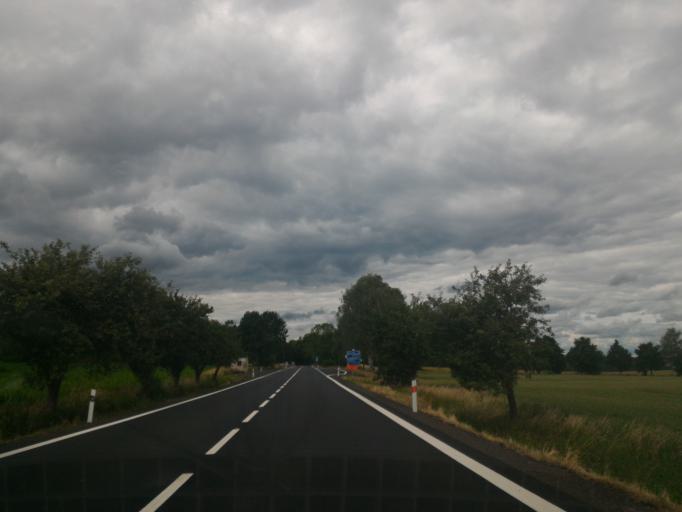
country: CZ
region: Vysocina
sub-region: Okres Pelhrimov
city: Zeliv
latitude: 49.5452
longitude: 15.1569
